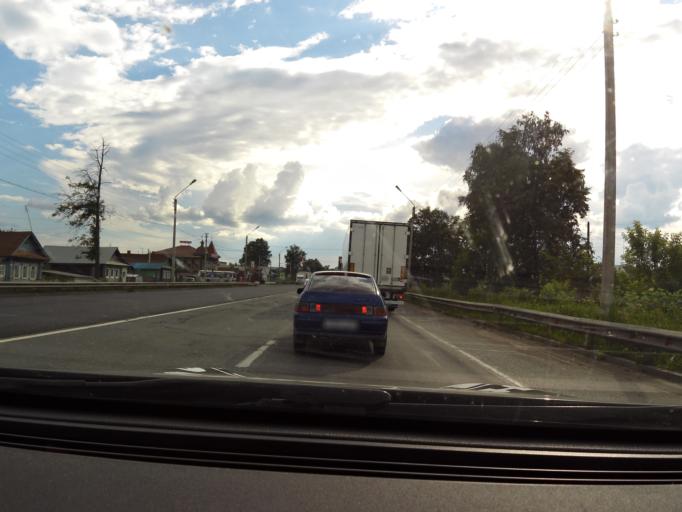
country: RU
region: Vladimir
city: Gorokhovets
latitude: 56.1985
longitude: 42.7040
